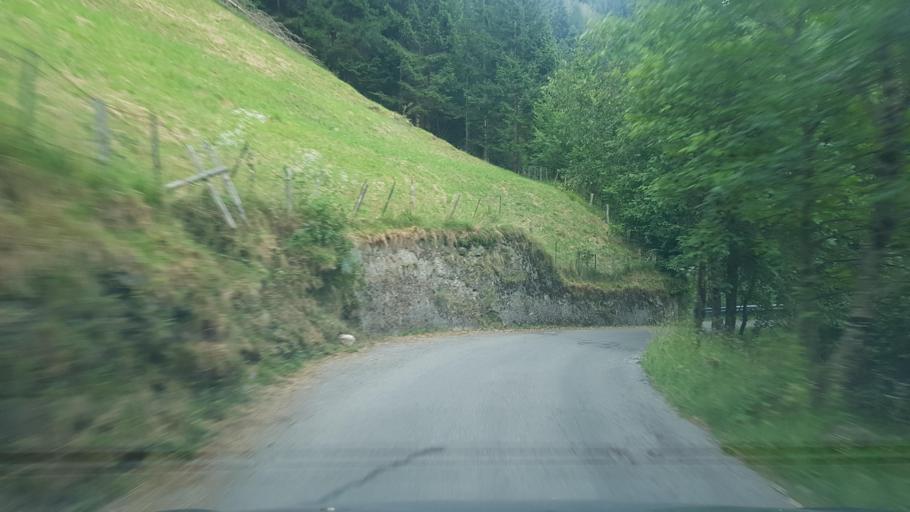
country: IT
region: Friuli Venezia Giulia
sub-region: Provincia di Udine
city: Paularo
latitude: 46.5434
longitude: 13.1228
